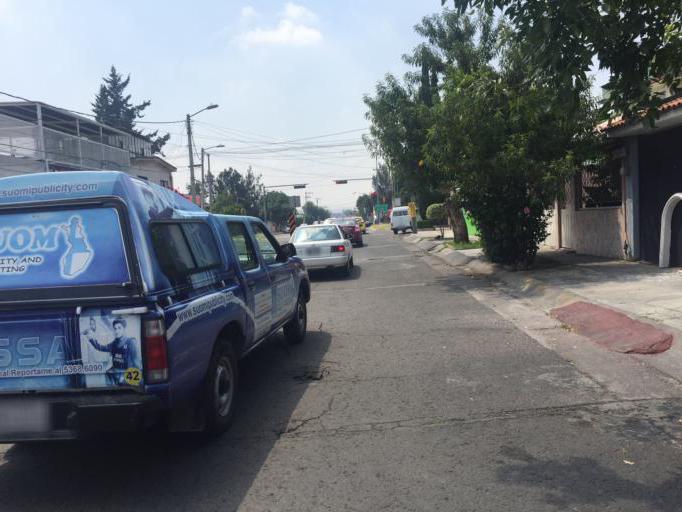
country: MX
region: Mexico
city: Cuautitlan Izcalli
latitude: 19.6490
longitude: -99.2145
